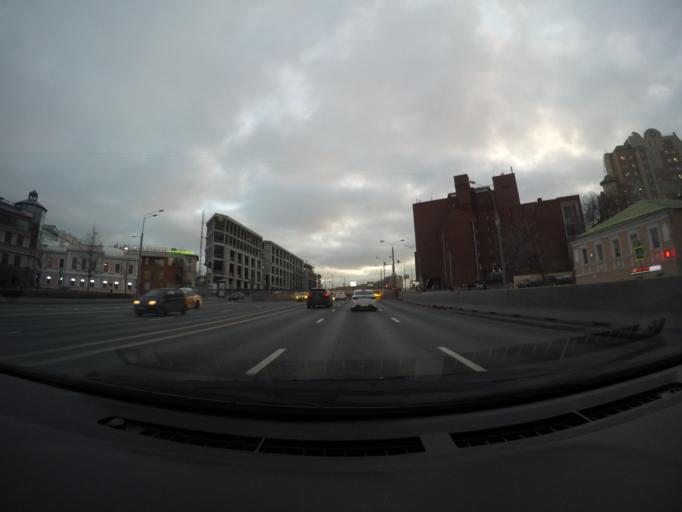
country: RU
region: Moscow
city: Taganskiy
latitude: 55.7445
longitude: 37.6550
